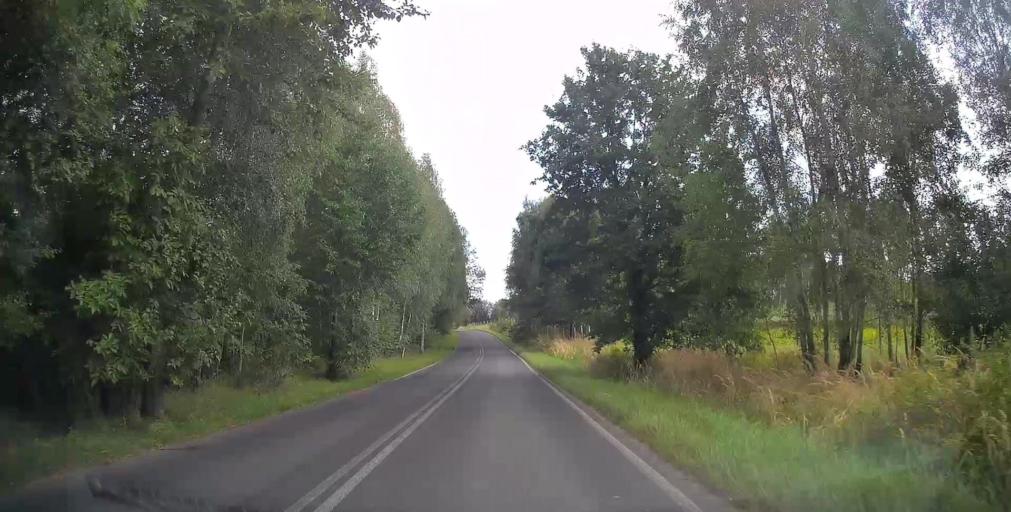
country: PL
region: Lesser Poland Voivodeship
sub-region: Powiat chrzanowski
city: Grojec
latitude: 50.0766
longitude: 19.5558
